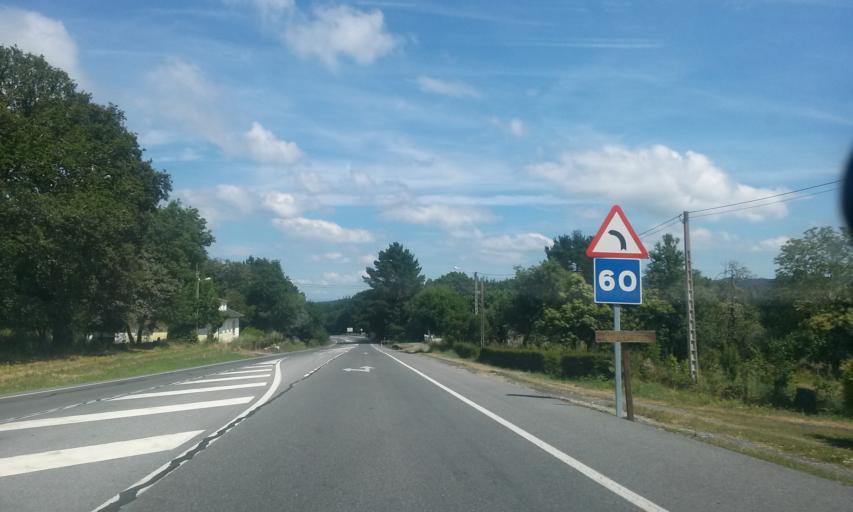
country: ES
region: Galicia
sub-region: Provincia de Lugo
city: Guitiriz
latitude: 43.1779
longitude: -7.8183
